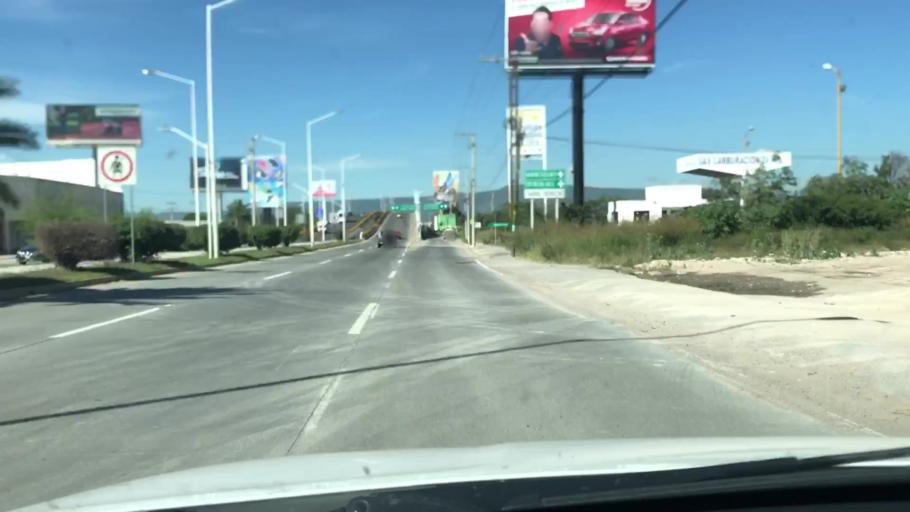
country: MX
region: Guanajuato
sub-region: San Francisco del Rincon
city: Estacion de San Francisco
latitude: 21.0366
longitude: -101.8193
